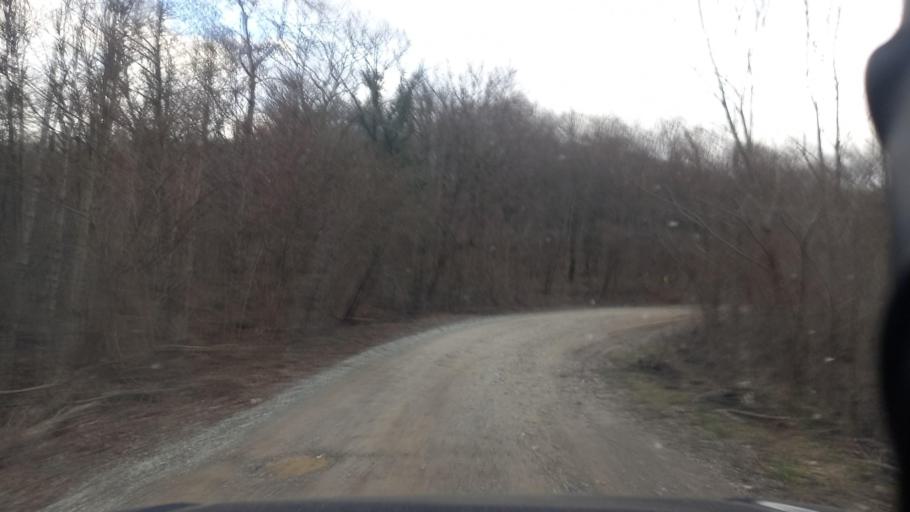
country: RU
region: Krasnodarskiy
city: Lermontovo
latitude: 44.4749
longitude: 38.8099
